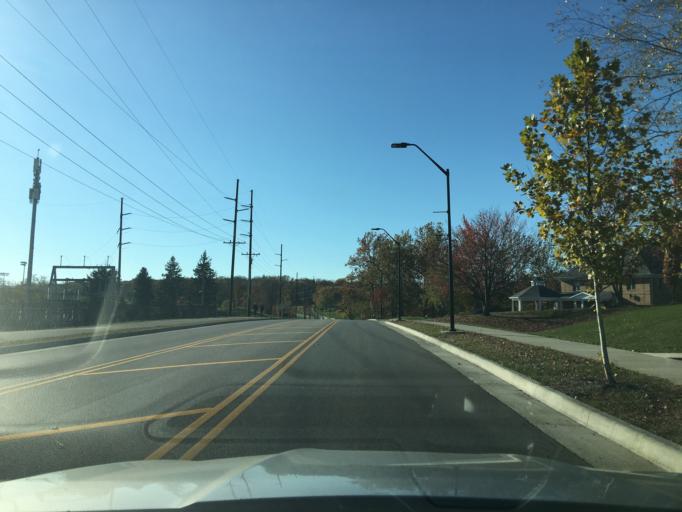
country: US
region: Indiana
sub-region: Tippecanoe County
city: West Lafayette
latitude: 40.4316
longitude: -86.9259
